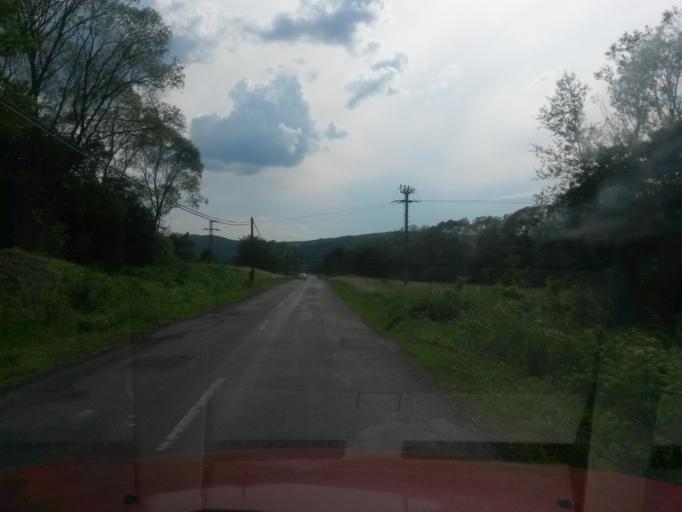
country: SK
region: Presovsky
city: Snina
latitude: 49.1082
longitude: 22.0711
